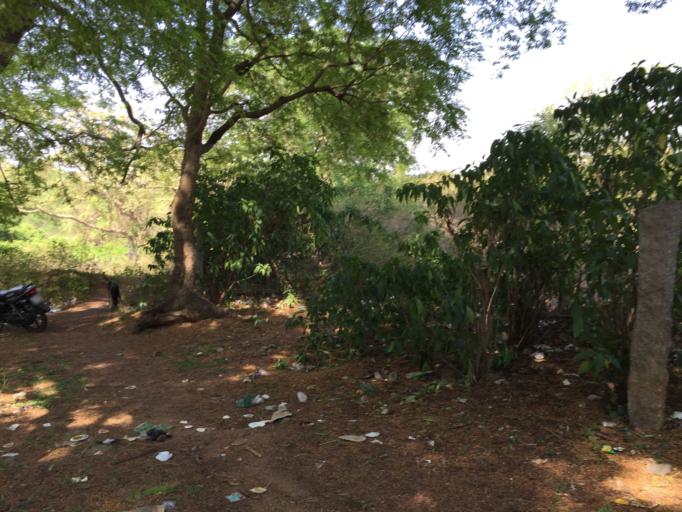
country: IN
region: Karnataka
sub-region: Ramanagara
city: Magadi
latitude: 12.9170
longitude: 77.2989
